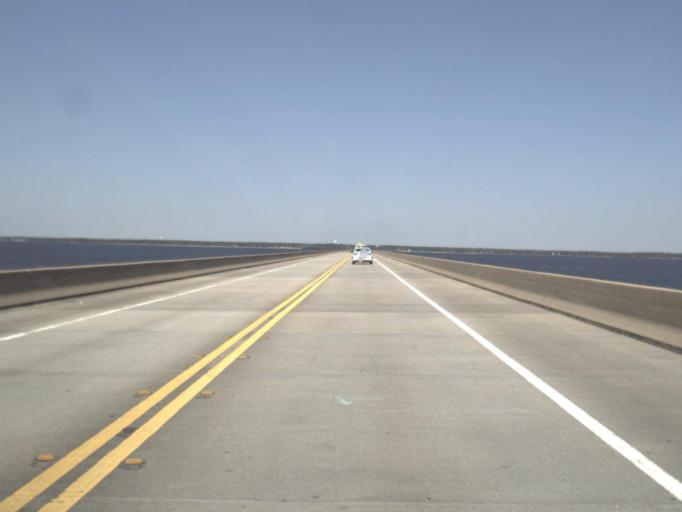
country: US
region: Florida
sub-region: Walton County
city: Miramar Beach
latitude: 30.4127
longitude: -86.4228
